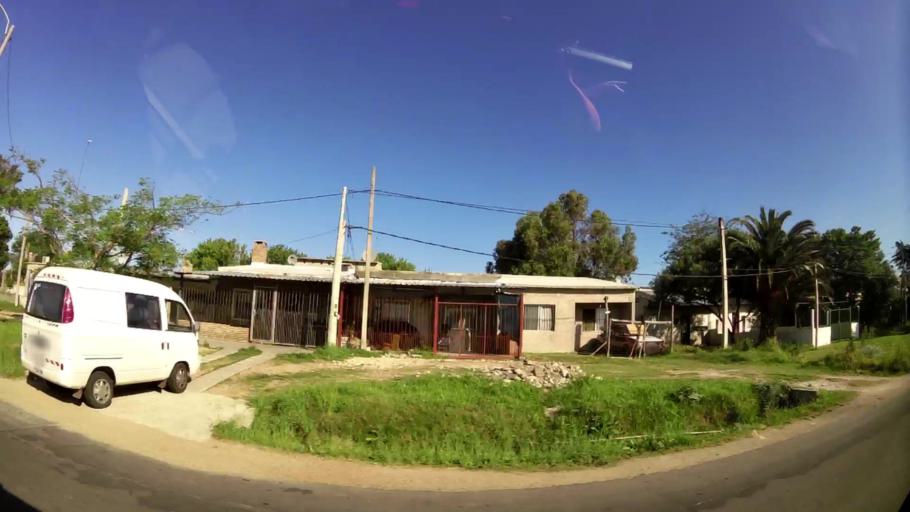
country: UY
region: Canelones
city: La Paz
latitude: -34.8223
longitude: -56.1781
